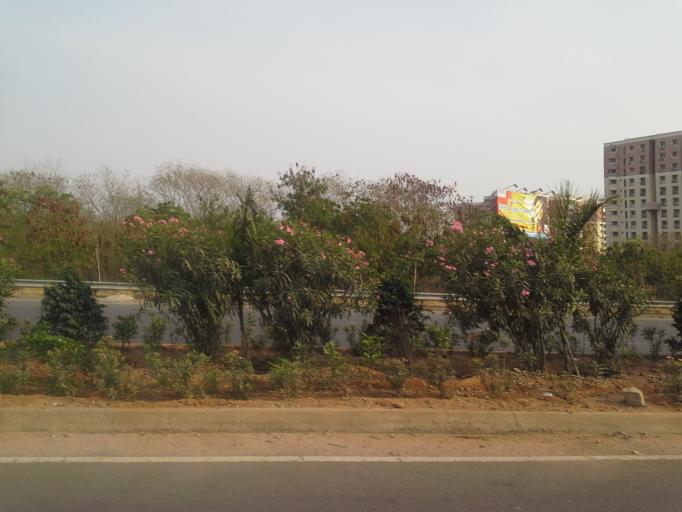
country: IN
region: Telangana
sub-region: Rangareddi
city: Kukatpalli
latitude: 17.4355
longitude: 78.3614
